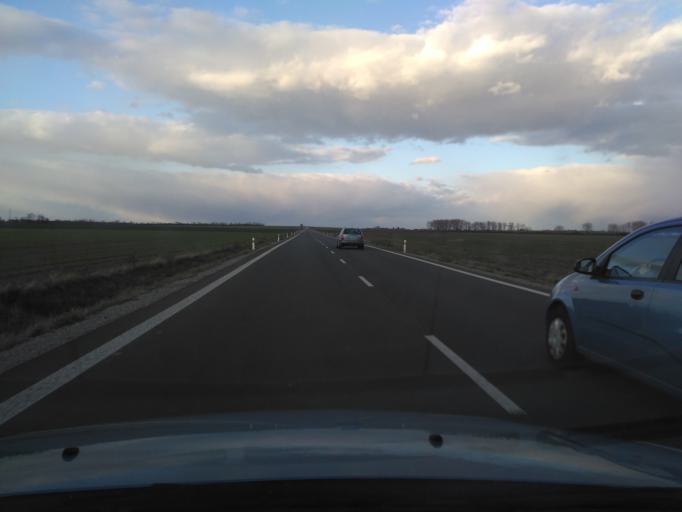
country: SK
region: Kosicky
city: Trebisov
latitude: 48.5530
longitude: 21.6943
